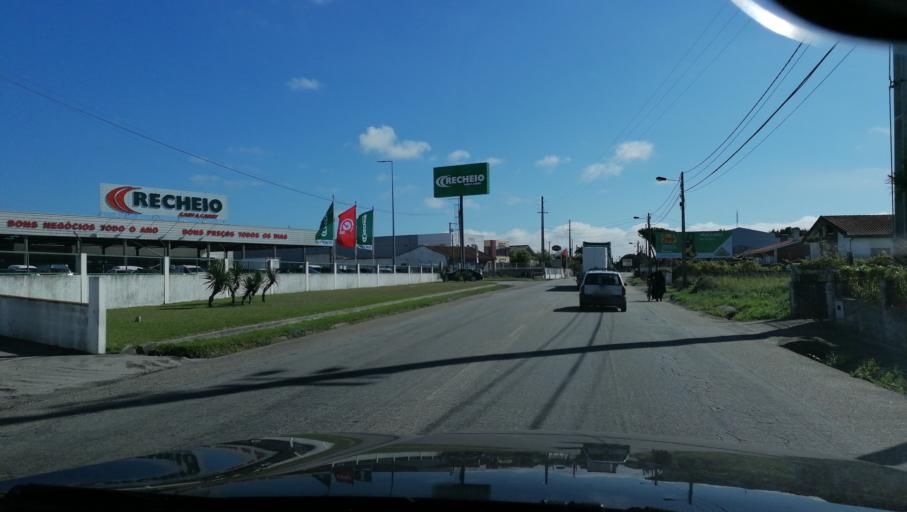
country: PT
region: Aveiro
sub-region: Aveiro
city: Aveiro
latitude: 40.6735
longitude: -8.6038
